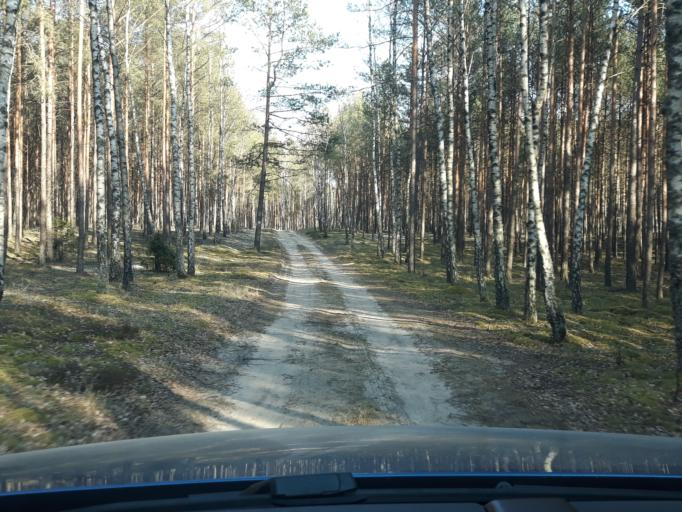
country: PL
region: Pomeranian Voivodeship
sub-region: Powiat bytowski
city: Lipnica
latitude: 53.9187
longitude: 17.4624
